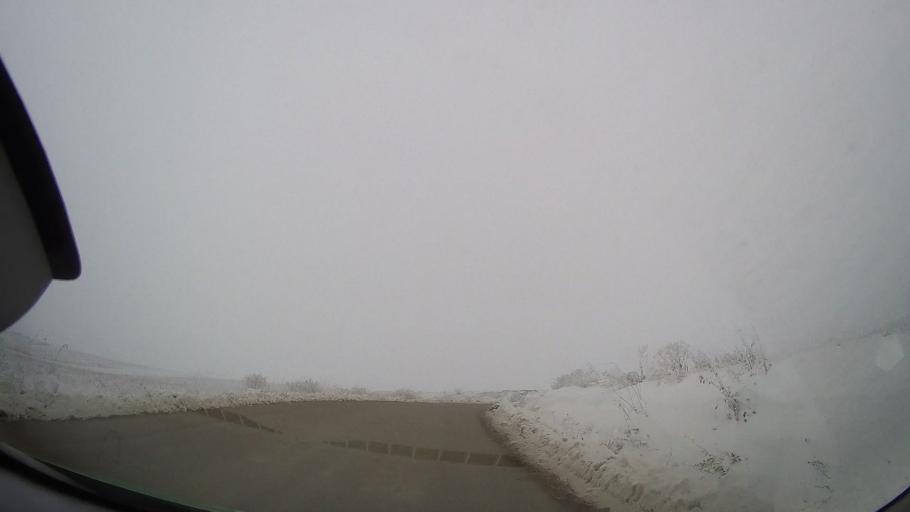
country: RO
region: Iasi
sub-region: Comuna Tansa
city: Suhulet
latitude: 46.8844
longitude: 27.2753
